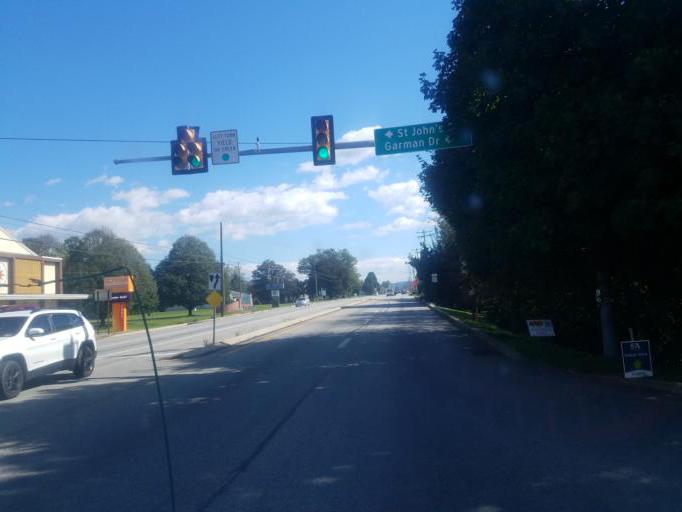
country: US
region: Pennsylvania
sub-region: Franklin County
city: Guilford
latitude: 39.9224
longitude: -77.6010
